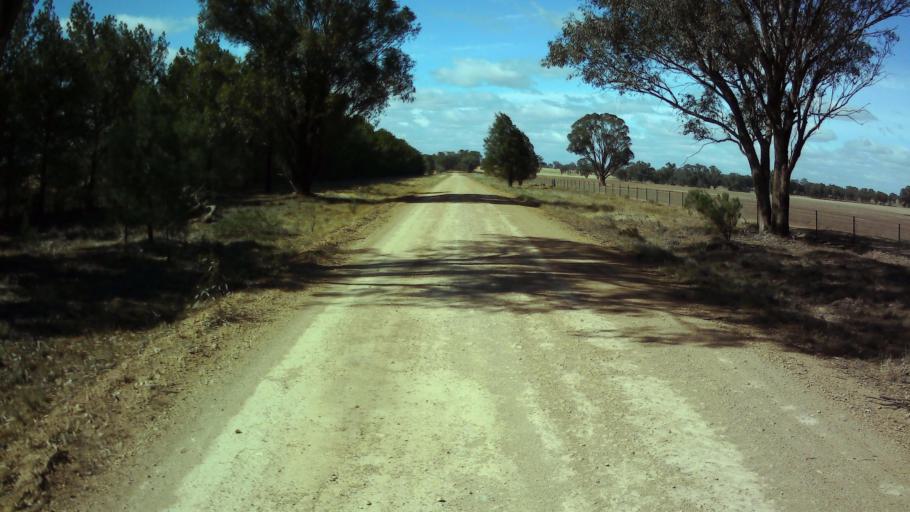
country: AU
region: New South Wales
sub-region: Weddin
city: Grenfell
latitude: -34.0574
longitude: 148.3127
